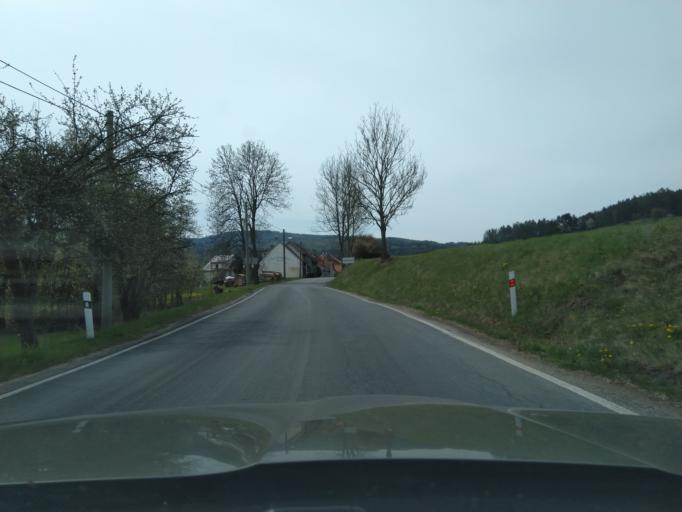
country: CZ
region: Plzensky
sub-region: Okres Klatovy
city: Susice
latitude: 49.2328
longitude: 13.5791
